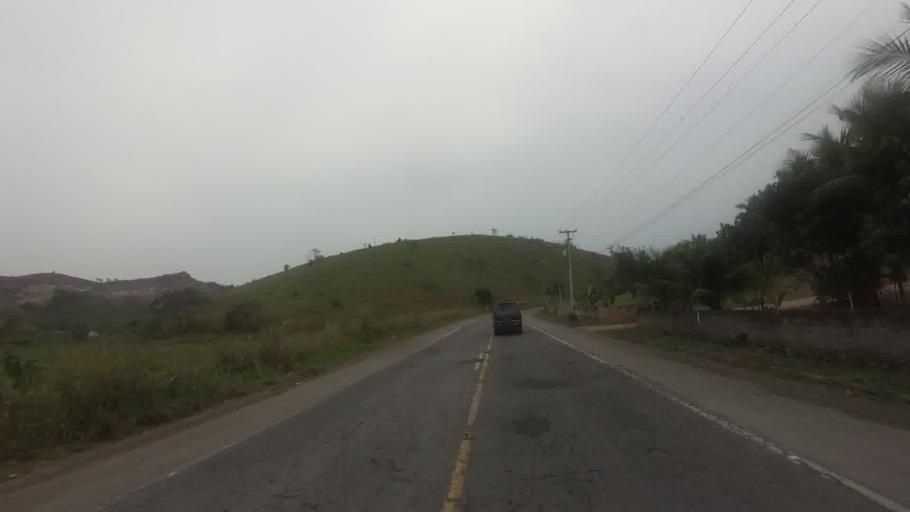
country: BR
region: Rio de Janeiro
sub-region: Santo Antonio De Padua
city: Santo Antonio de Padua
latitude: -21.6035
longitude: -42.2404
